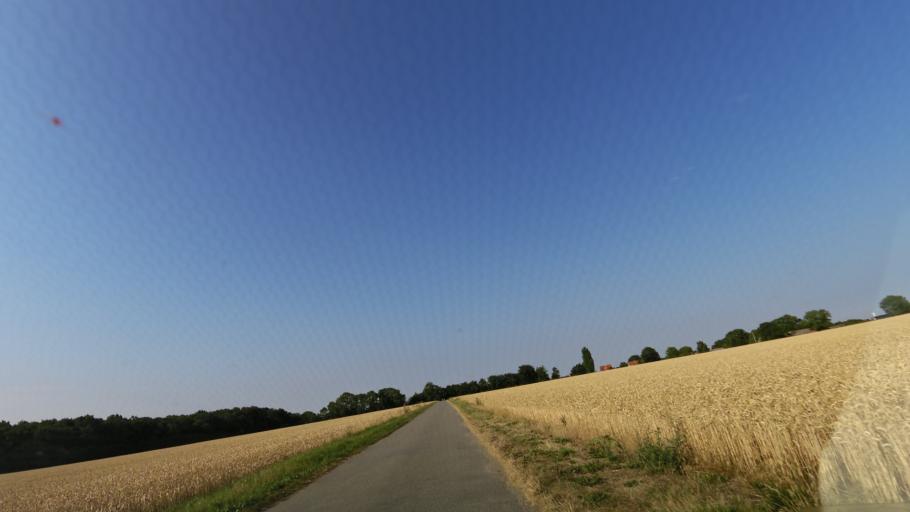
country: DK
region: South Denmark
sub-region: Nordfyns Kommune
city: Otterup
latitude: 55.5874
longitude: 10.3954
